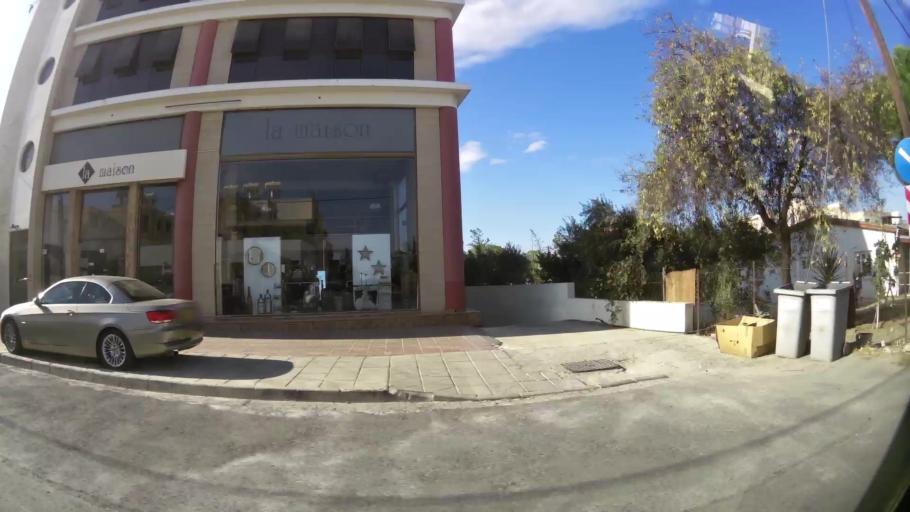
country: CY
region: Lefkosia
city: Nicosia
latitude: 35.1379
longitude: 33.3485
